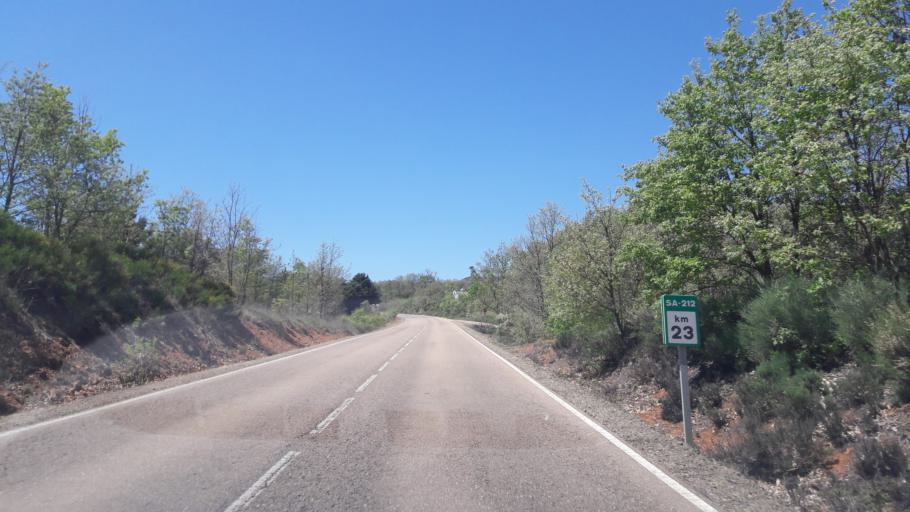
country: ES
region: Castille and Leon
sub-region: Provincia de Salamanca
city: Linares de Riofrio
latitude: 40.5875
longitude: -5.9063
